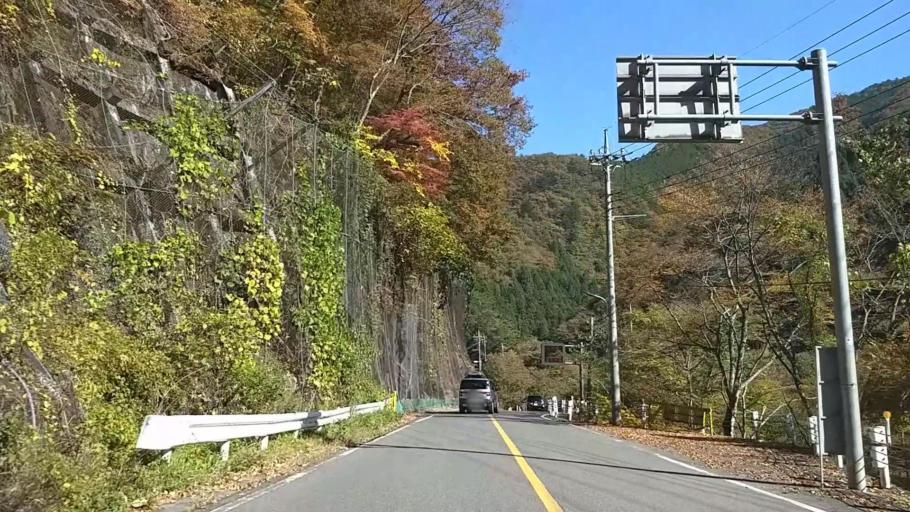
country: JP
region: Yamanashi
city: Otsuki
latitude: 35.7624
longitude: 138.9913
